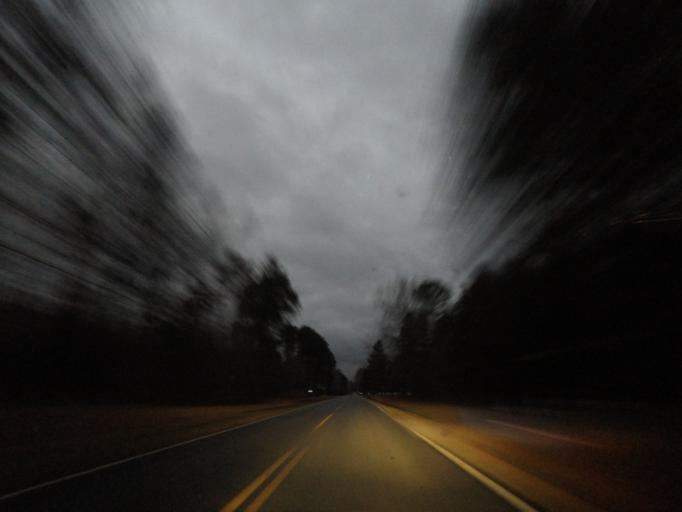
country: US
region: North Carolina
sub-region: Orange County
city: Hillsborough
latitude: 36.0559
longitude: -79.0042
